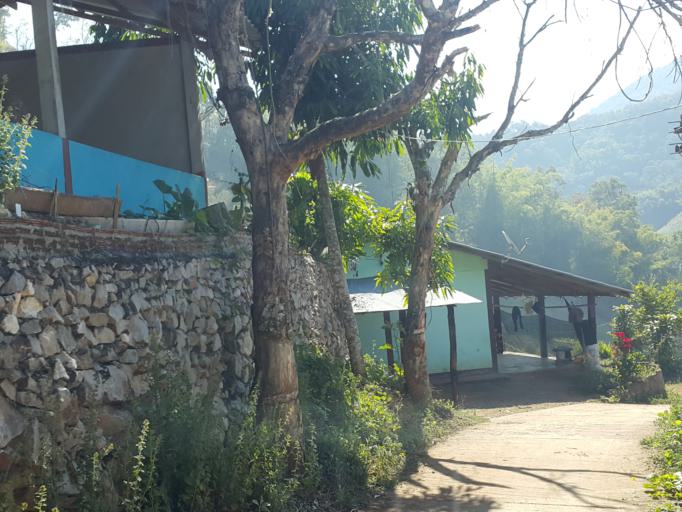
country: TH
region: Chiang Mai
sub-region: Amphoe Chiang Dao
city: Chiang Dao
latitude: 19.5218
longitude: 98.8629
